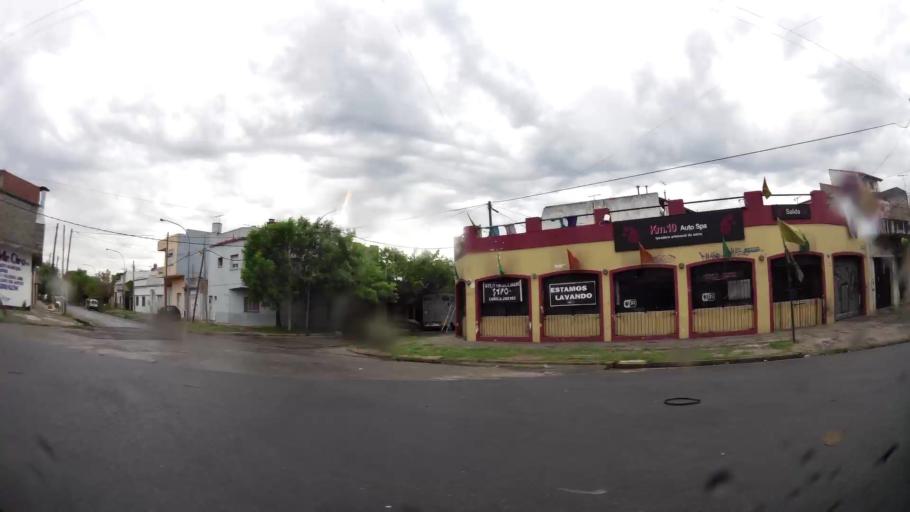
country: AR
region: Buenos Aires
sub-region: Partido de Lanus
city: Lanus
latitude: -34.6841
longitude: -58.4049
